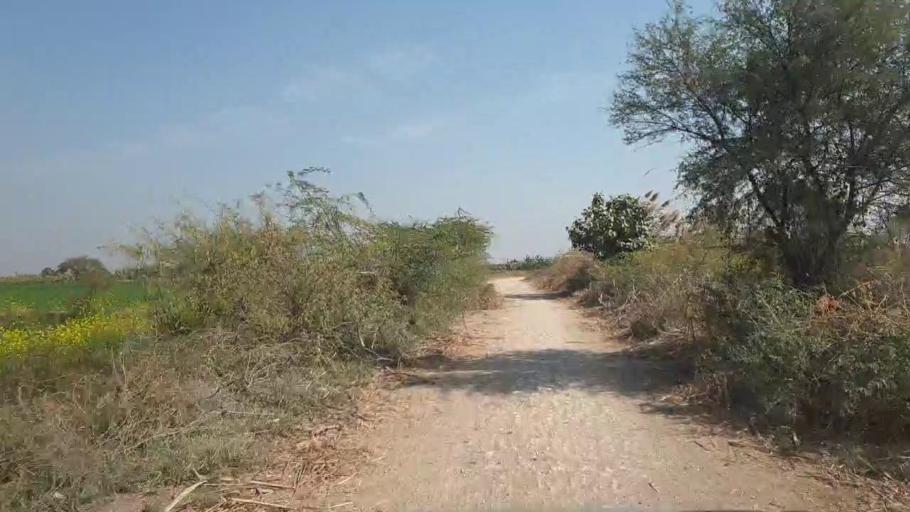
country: PK
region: Sindh
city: Chambar
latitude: 25.3505
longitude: 68.8274
